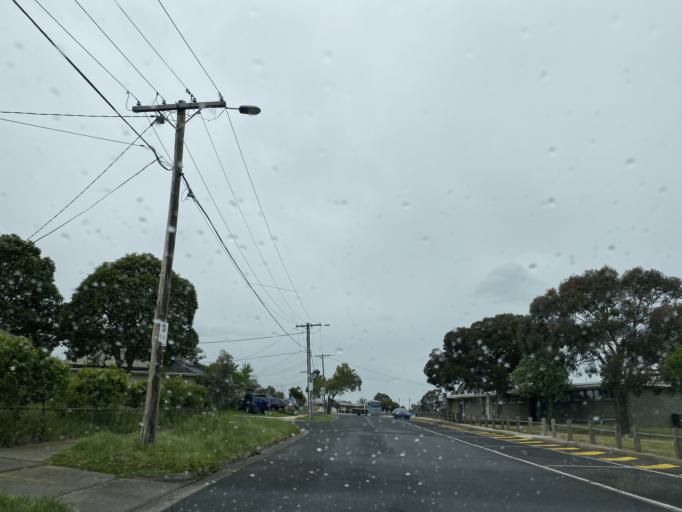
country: AU
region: Victoria
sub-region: Moreland
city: Fawkner
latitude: -37.7138
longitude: 144.9722
